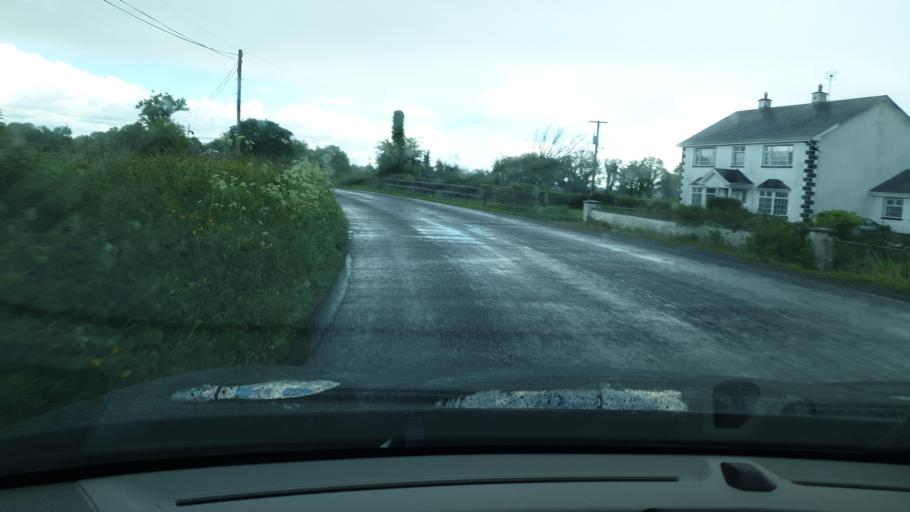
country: IE
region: Leinster
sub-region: Laois
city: Mountmellick
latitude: 53.1067
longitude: -7.3894
